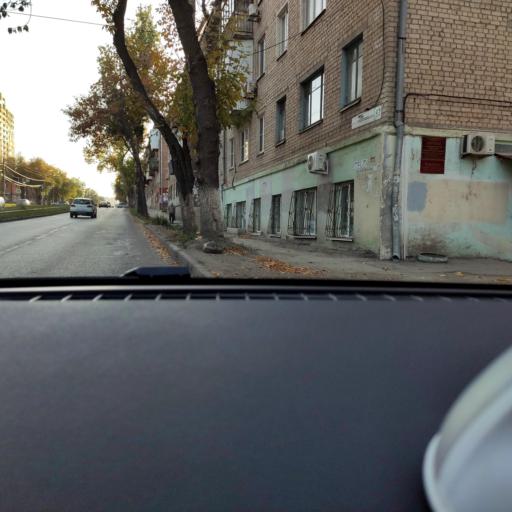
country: RU
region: Samara
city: Samara
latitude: 53.2221
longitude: 50.2322
